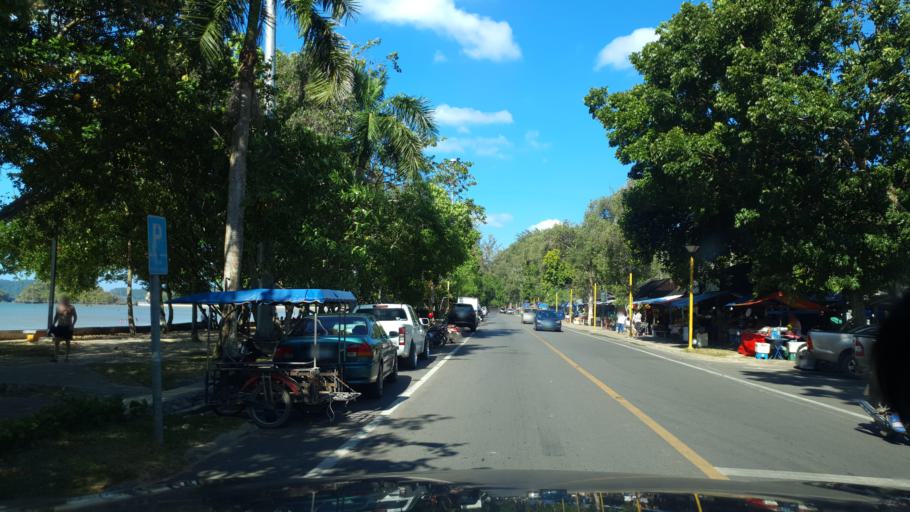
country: TH
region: Phangnga
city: Ban Ao Nang
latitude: 8.0444
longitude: 98.8070
